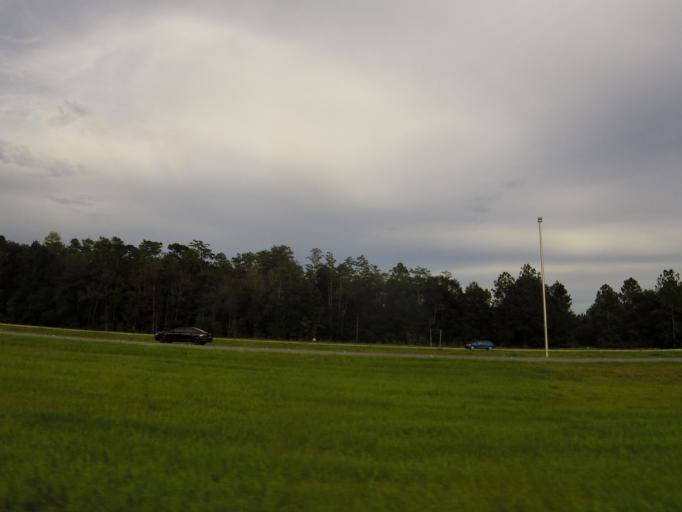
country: US
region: Florida
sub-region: Clay County
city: Lakeside
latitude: 30.1256
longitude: -81.8306
